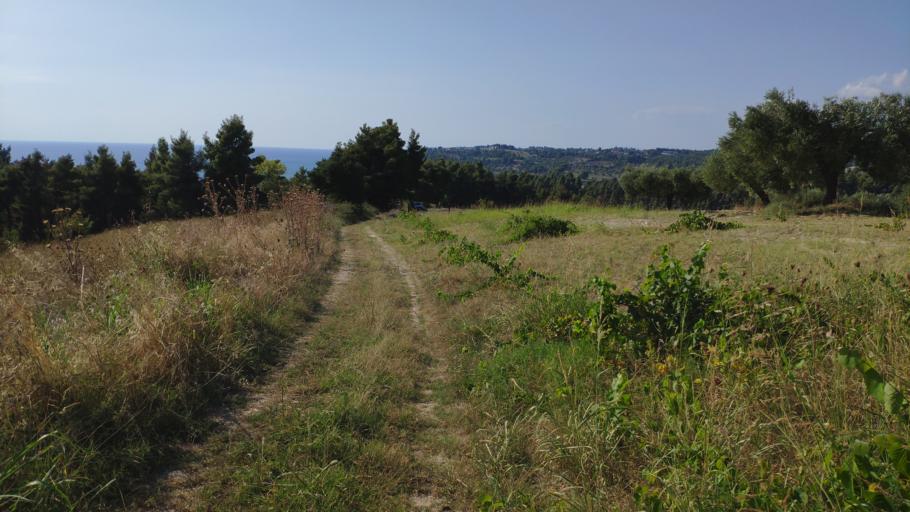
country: GR
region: Central Macedonia
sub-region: Nomos Chalkidikis
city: Kassandreia
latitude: 40.0292
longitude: 23.3686
